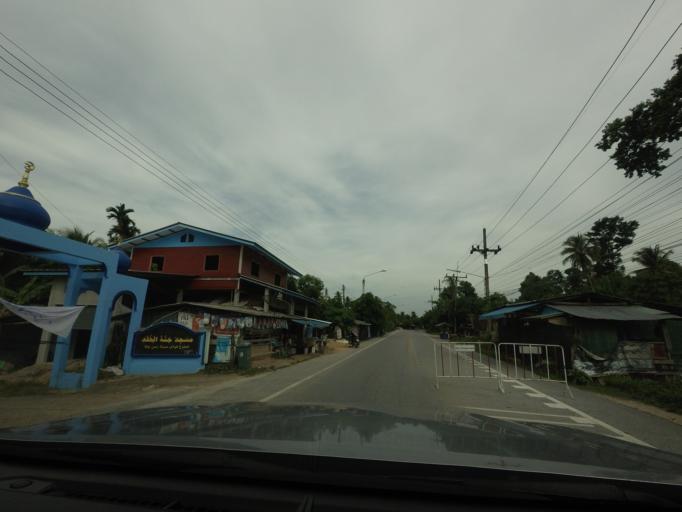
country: TH
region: Yala
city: Raman
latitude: 6.4560
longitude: 101.4454
